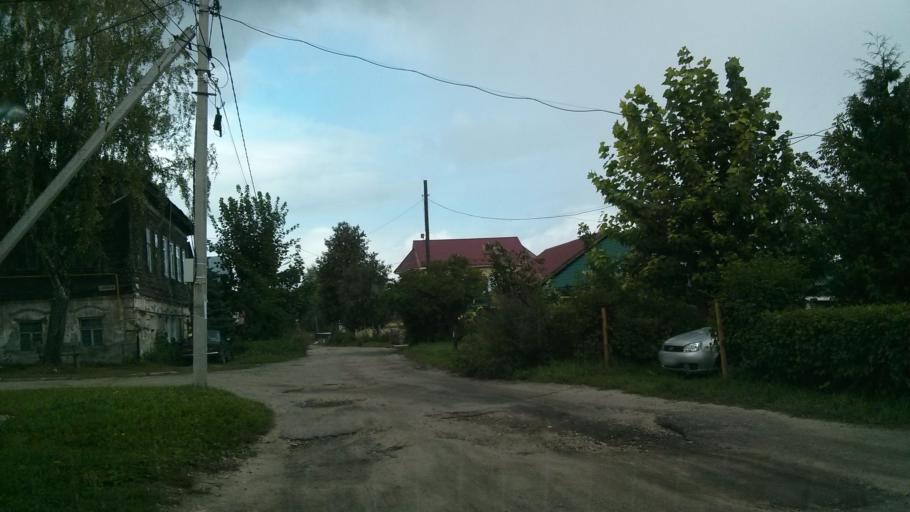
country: RU
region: Vladimir
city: Murom
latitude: 55.5746
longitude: 42.0655
